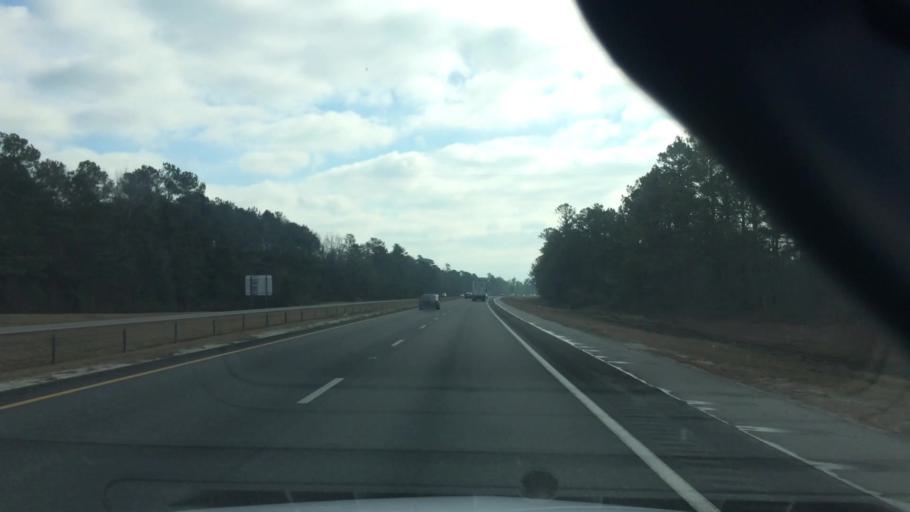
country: US
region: North Carolina
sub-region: Pender County
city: Burgaw
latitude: 34.5649
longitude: -77.8974
